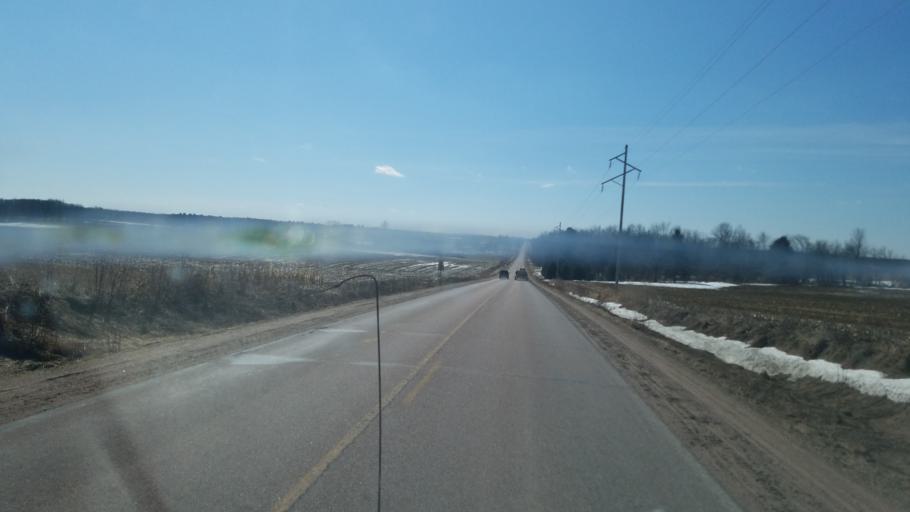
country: US
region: Wisconsin
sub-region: Clark County
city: Loyal
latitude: 44.5773
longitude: -90.3959
